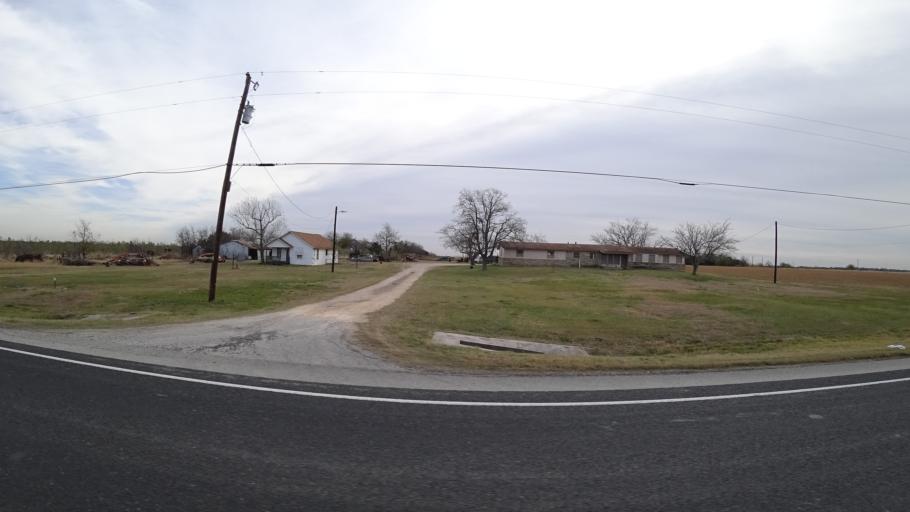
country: US
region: Texas
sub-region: Travis County
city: Onion Creek
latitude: 30.1352
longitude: -97.7063
